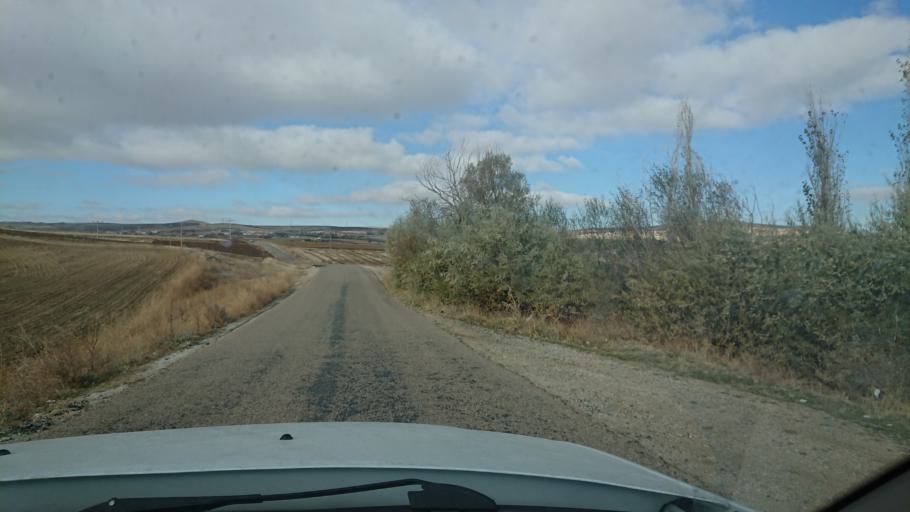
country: TR
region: Aksaray
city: Agacoren
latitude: 38.8190
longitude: 33.9776
